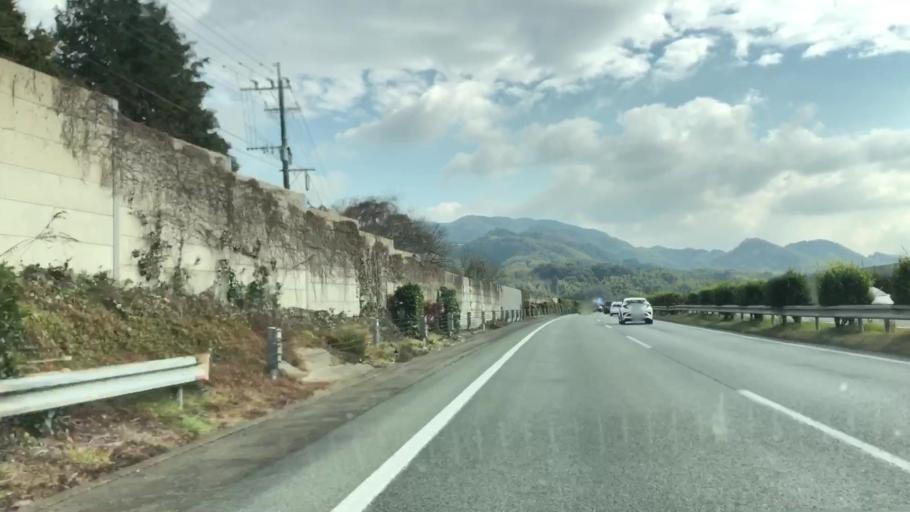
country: JP
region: Fukuoka
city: Setakamachi-takayanagi
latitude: 33.1170
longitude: 130.5266
